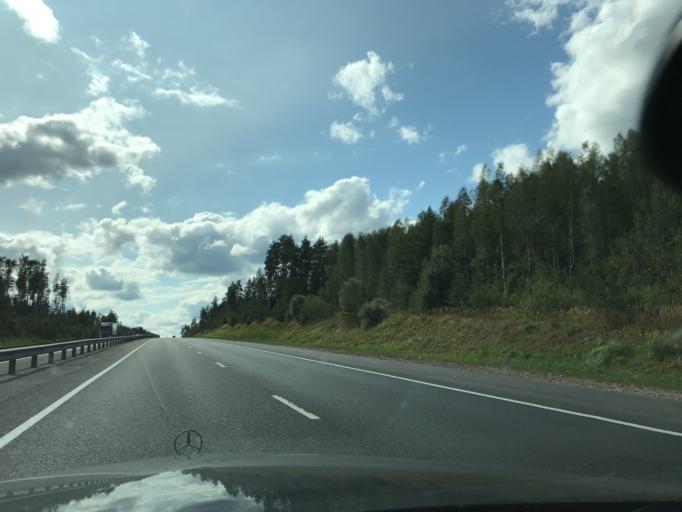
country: RU
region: Vladimir
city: Sudogda
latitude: 56.1214
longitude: 40.8580
